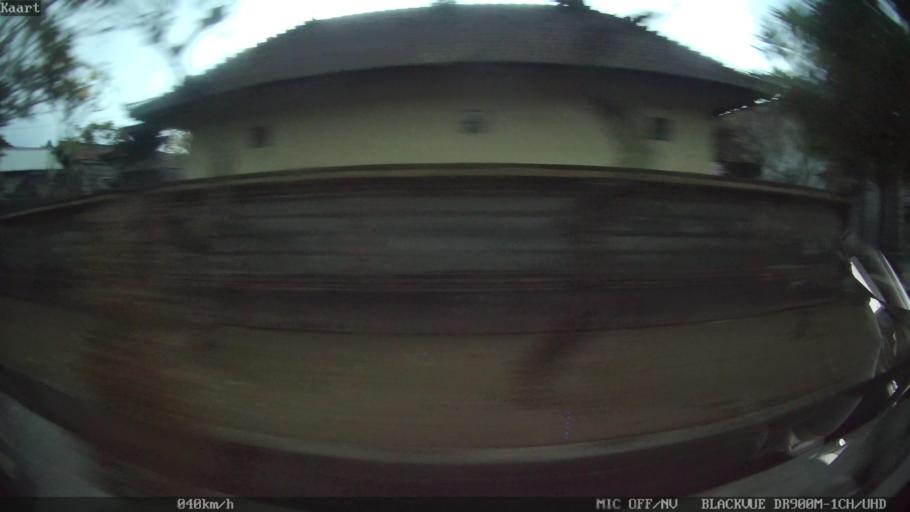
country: ID
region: Bali
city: Banjar Pasekan
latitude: -8.6216
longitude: 115.2731
